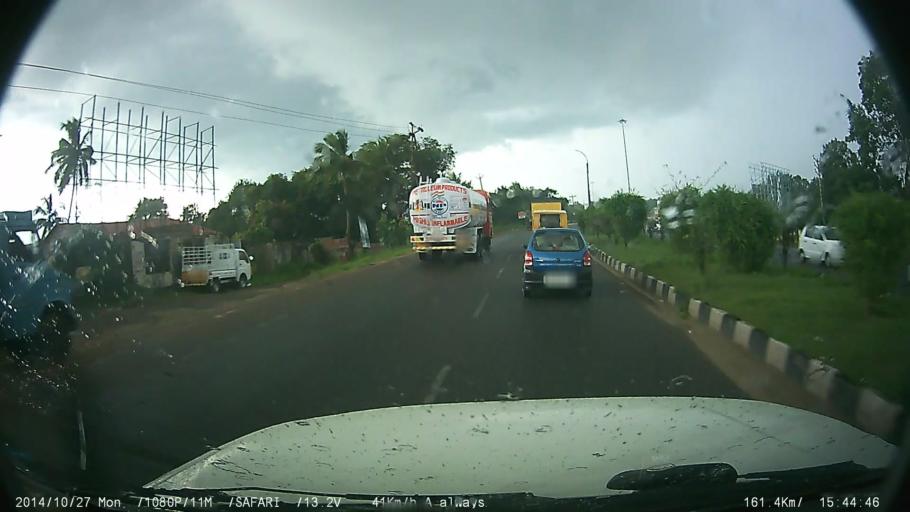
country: IN
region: Kerala
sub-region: Ernakulam
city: Angamali
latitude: 10.2058
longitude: 76.3822
